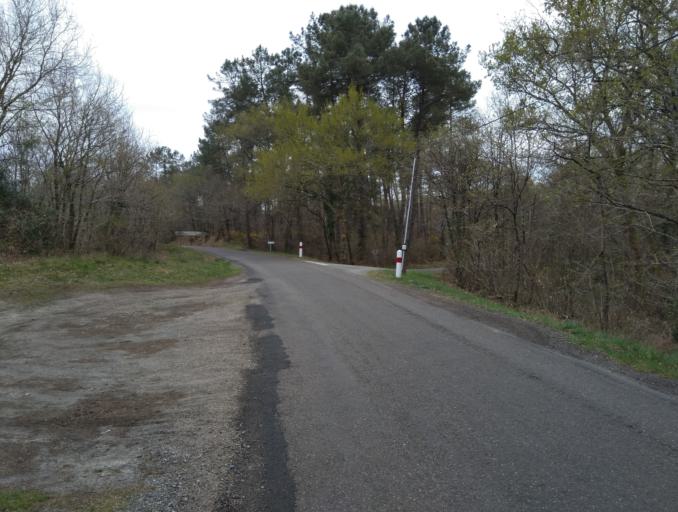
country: FR
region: Aquitaine
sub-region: Departement des Landes
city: Saint-Geours-de-Maremne
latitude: 43.7116
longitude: -1.1877
